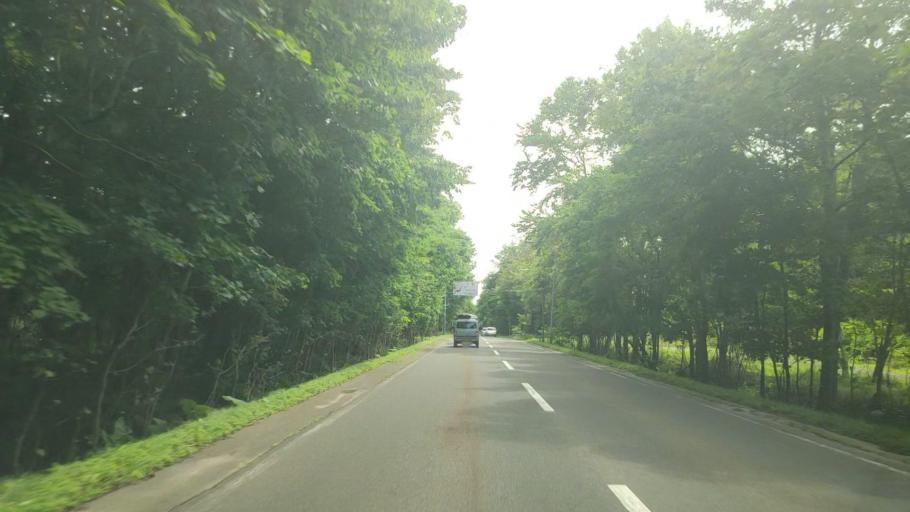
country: JP
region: Hokkaido
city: Tomakomai
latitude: 42.7726
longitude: 141.4402
